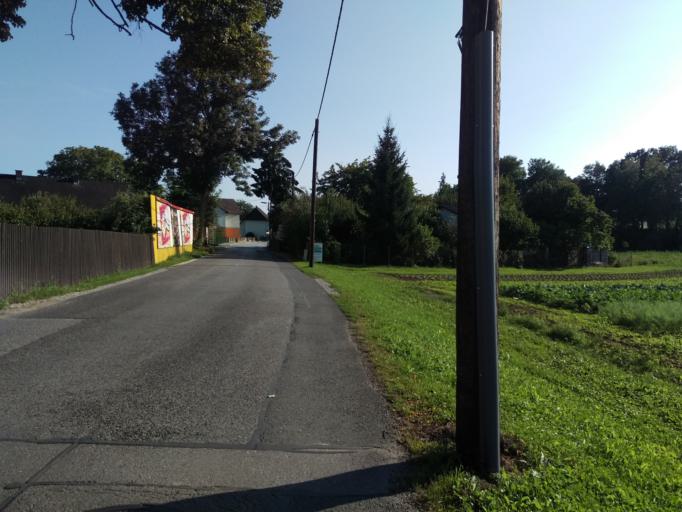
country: AT
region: Styria
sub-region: Politischer Bezirk Graz-Umgebung
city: Feldkirchen bei Graz
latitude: 47.0162
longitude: 15.4442
